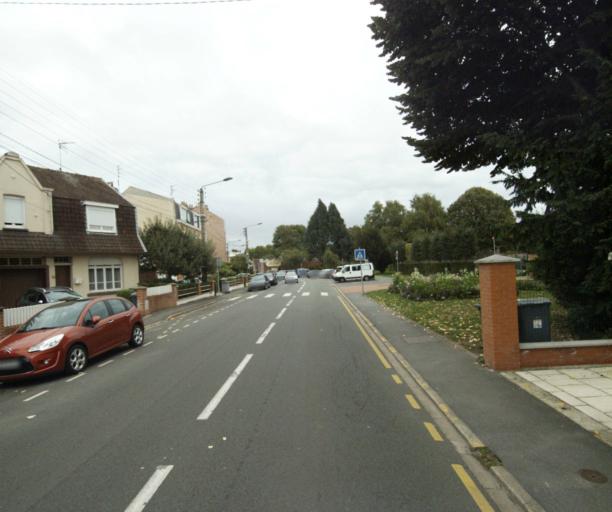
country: FR
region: Nord-Pas-de-Calais
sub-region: Departement du Nord
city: Lambersart
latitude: 50.6445
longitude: 3.0252
